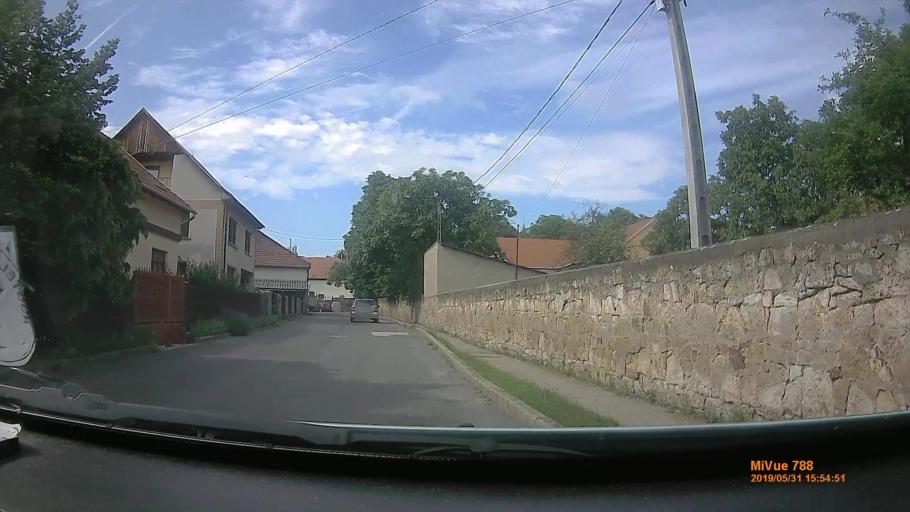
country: HU
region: Borsod-Abauj-Zemplen
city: Szerencs
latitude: 48.1619
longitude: 21.2000
